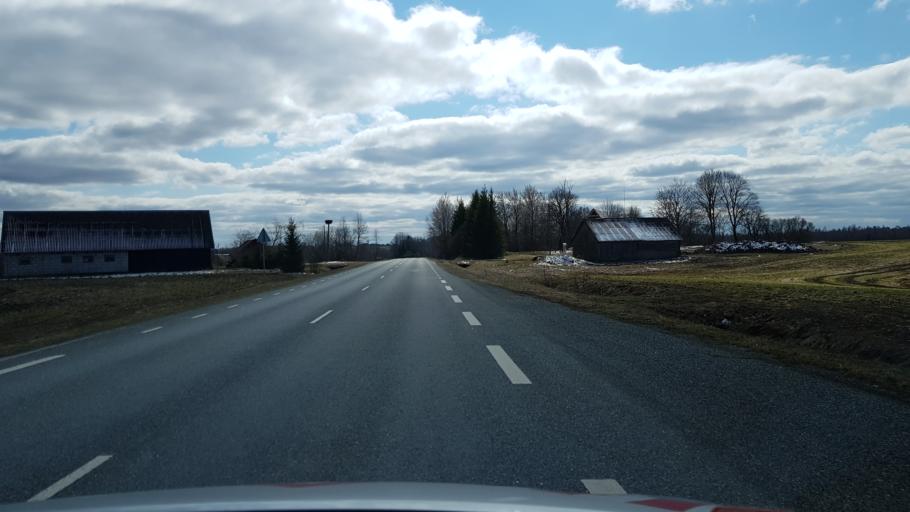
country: EE
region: Laeaene-Virumaa
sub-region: Kadrina vald
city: Kadrina
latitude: 59.3737
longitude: 26.1000
